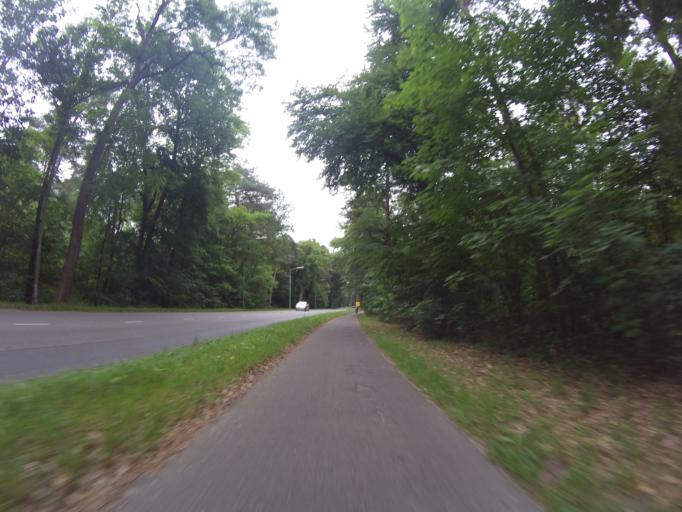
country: NL
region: Drenthe
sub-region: Gemeente Emmen
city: Emmen
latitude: 52.7901
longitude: 6.9051
